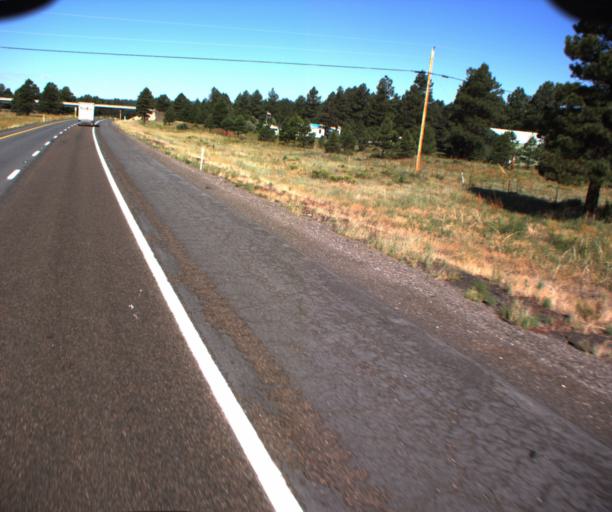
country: US
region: Arizona
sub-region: Coconino County
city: Parks
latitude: 35.2479
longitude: -111.9752
